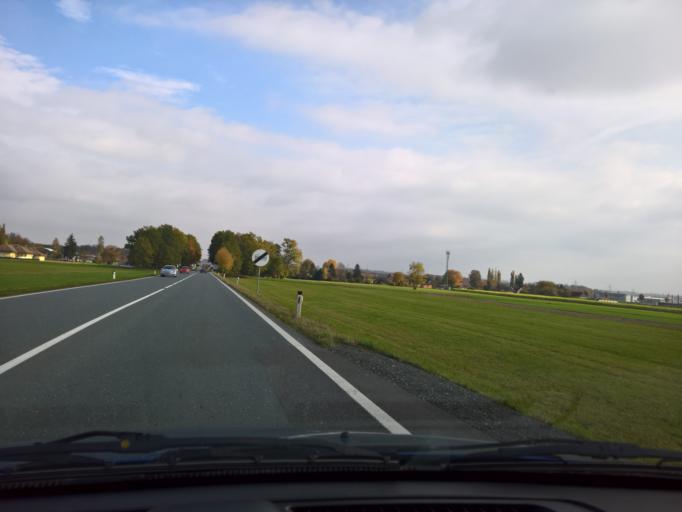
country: AT
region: Styria
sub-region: Politischer Bezirk Leibnitz
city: Kaindorf an der Sulm
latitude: 46.8016
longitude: 15.5495
